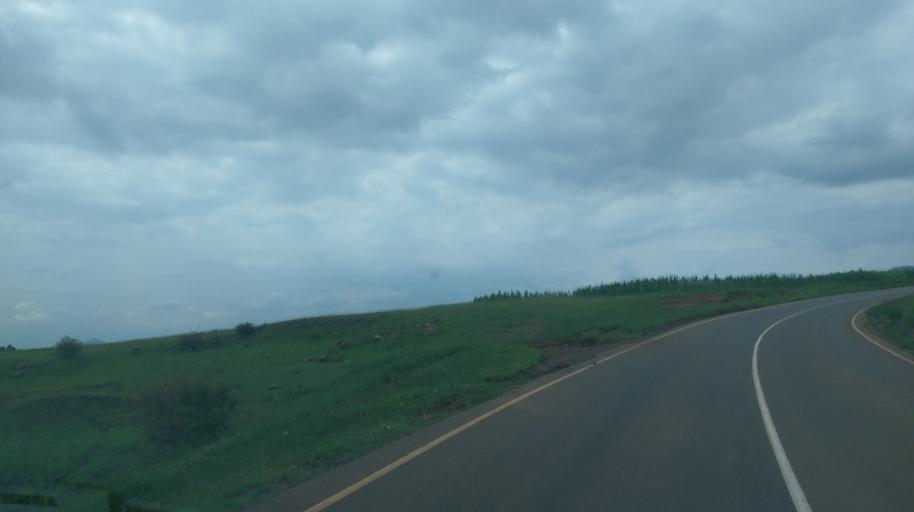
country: LS
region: Leribe
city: Leribe
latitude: -29.0343
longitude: 28.2527
